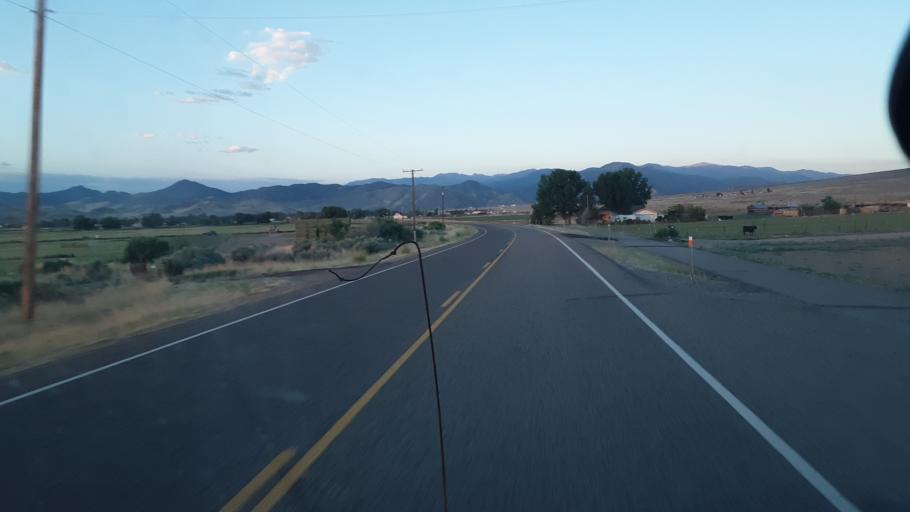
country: US
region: Utah
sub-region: Sevier County
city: Monroe
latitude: 38.6413
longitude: -112.2153
